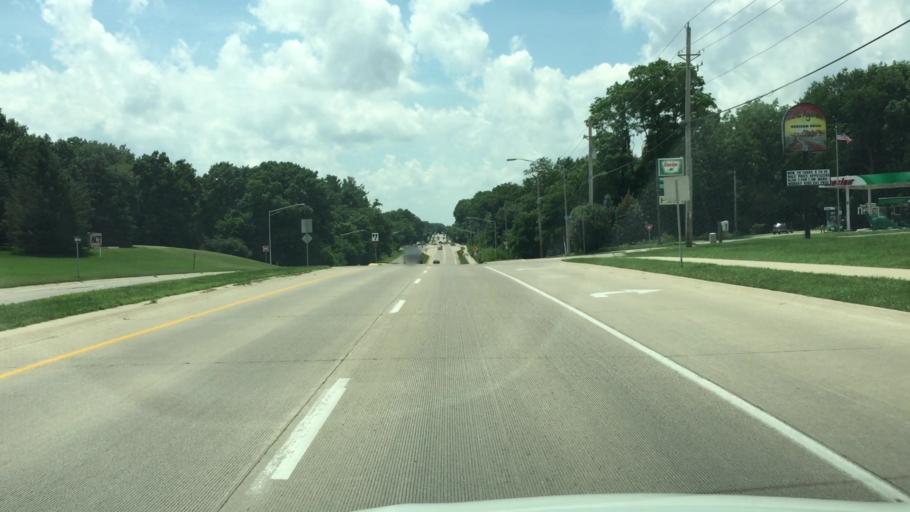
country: US
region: Iowa
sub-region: Johnson County
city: Iowa City
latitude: 41.6836
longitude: -91.5035
